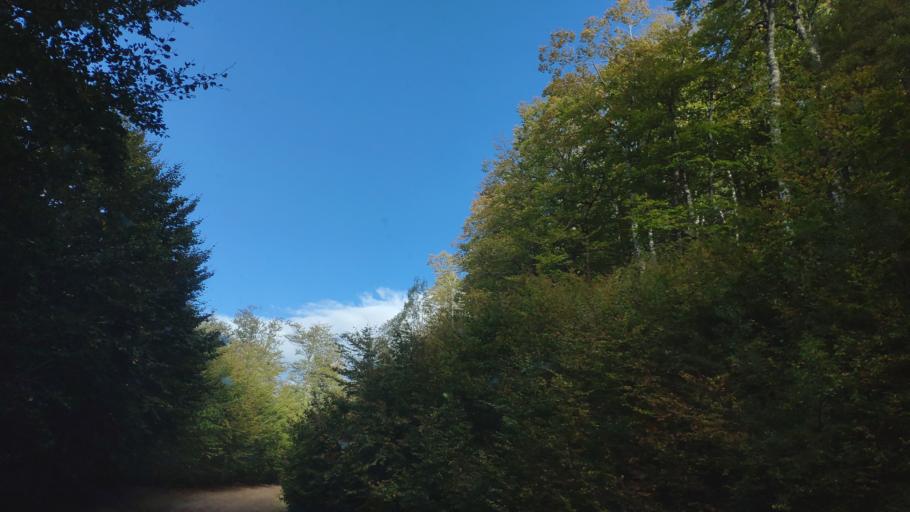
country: GR
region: West Macedonia
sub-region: Nomos Kastorias
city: Nestorio
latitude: 40.3228
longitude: 20.9070
